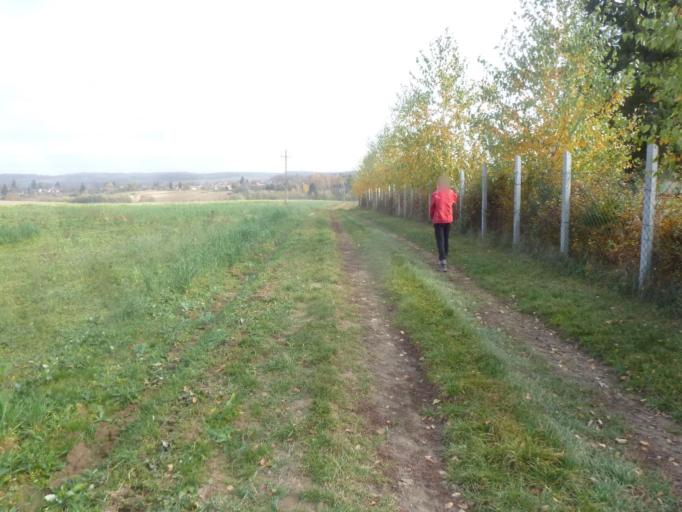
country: HU
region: Zala
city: Pacsa
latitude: 46.6231
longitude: 17.0502
